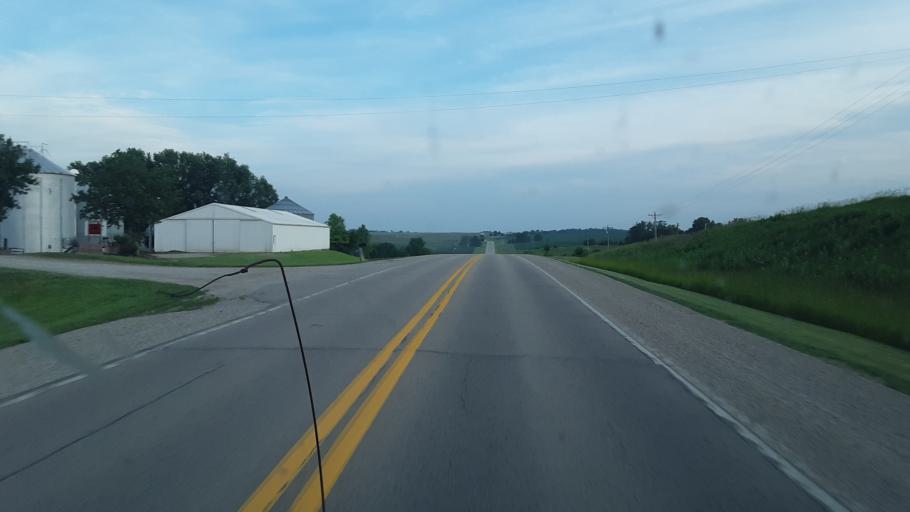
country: US
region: Iowa
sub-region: Benton County
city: Belle Plaine
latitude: 41.7903
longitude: -92.2792
